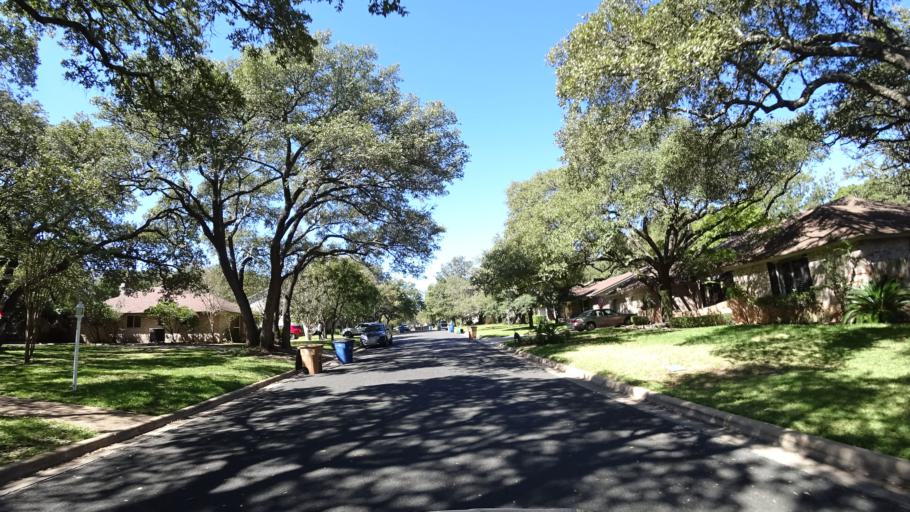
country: US
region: Texas
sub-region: Travis County
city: West Lake Hills
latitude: 30.3647
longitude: -97.7674
